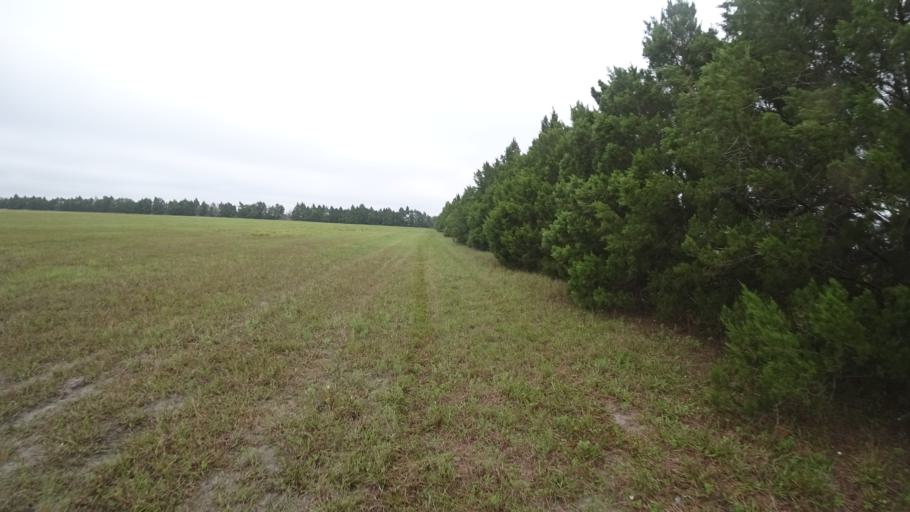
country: US
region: Florida
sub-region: Sarasota County
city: Warm Mineral Springs
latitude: 27.3079
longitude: -82.1497
